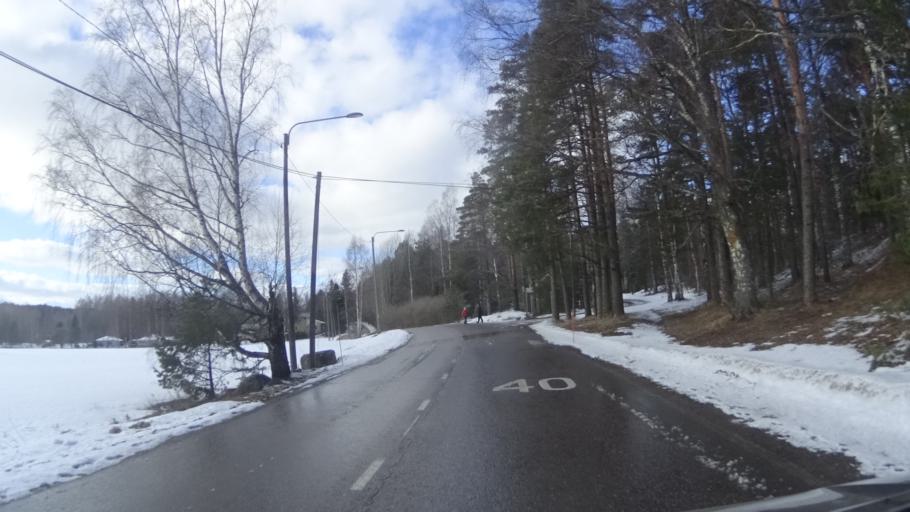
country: FI
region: Uusimaa
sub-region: Helsinki
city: Vantaa
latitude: 60.2518
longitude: 25.1715
